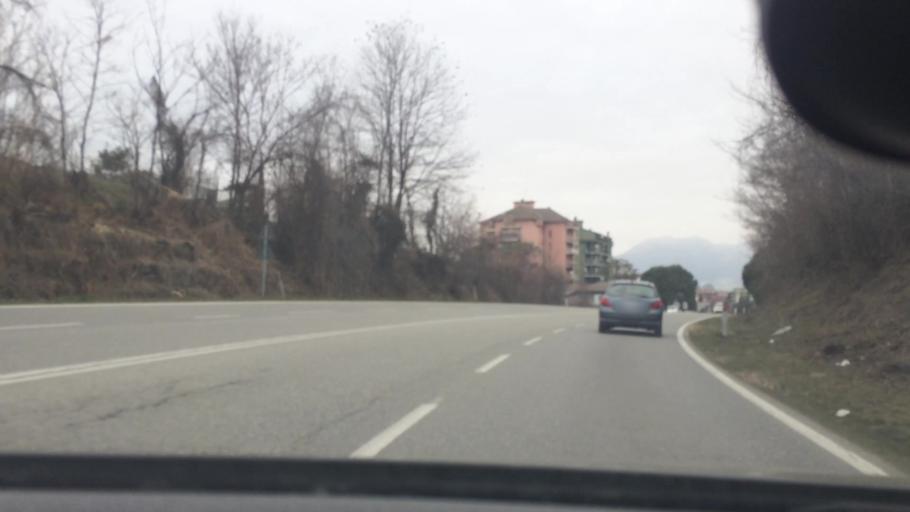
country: IT
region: Lombardy
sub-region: Provincia di Como
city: Inverigo
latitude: 45.7419
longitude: 9.2155
